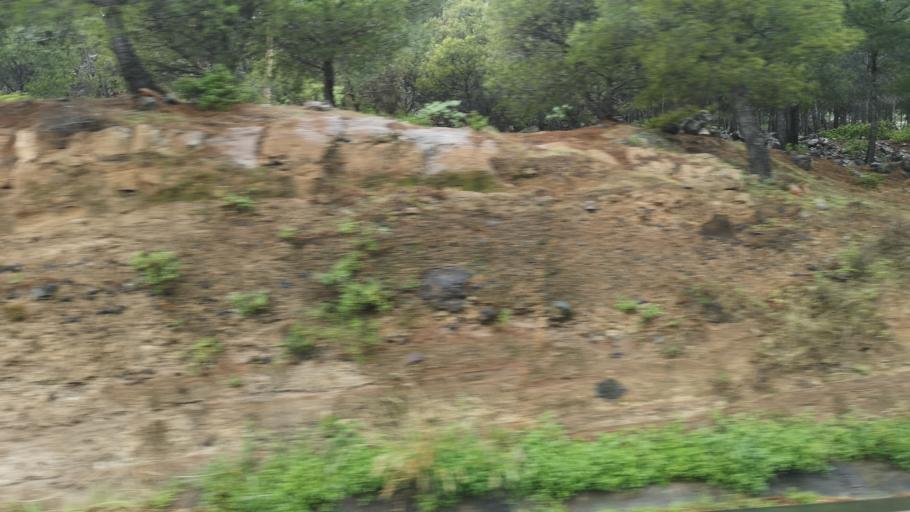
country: ES
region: Canary Islands
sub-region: Provincia de Santa Cruz de Tenerife
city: Alajero
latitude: 28.0848
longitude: -17.1997
